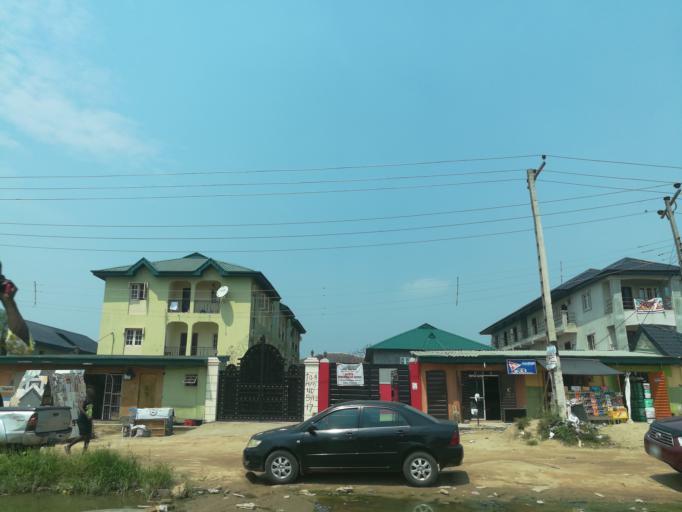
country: NG
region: Lagos
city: Ikorodu
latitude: 6.6380
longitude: 3.4815
